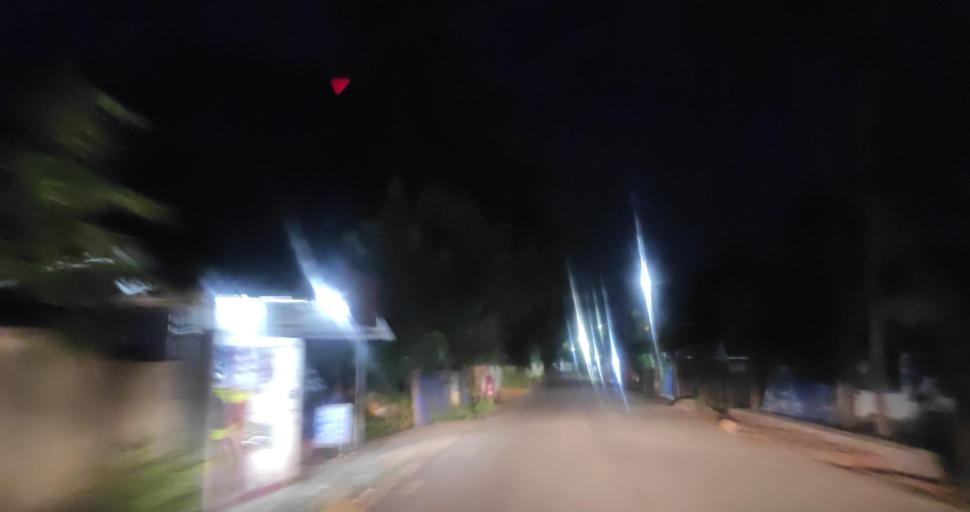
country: IN
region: Kerala
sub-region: Alappuzha
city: Vayalar
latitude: 9.6838
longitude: 76.3026
